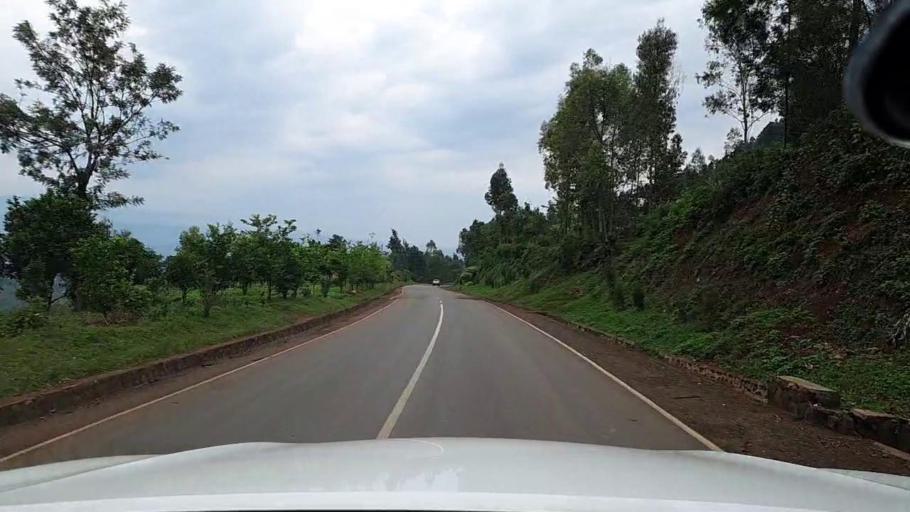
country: RW
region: Western Province
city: Cyangugu
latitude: -2.6530
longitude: 28.9694
